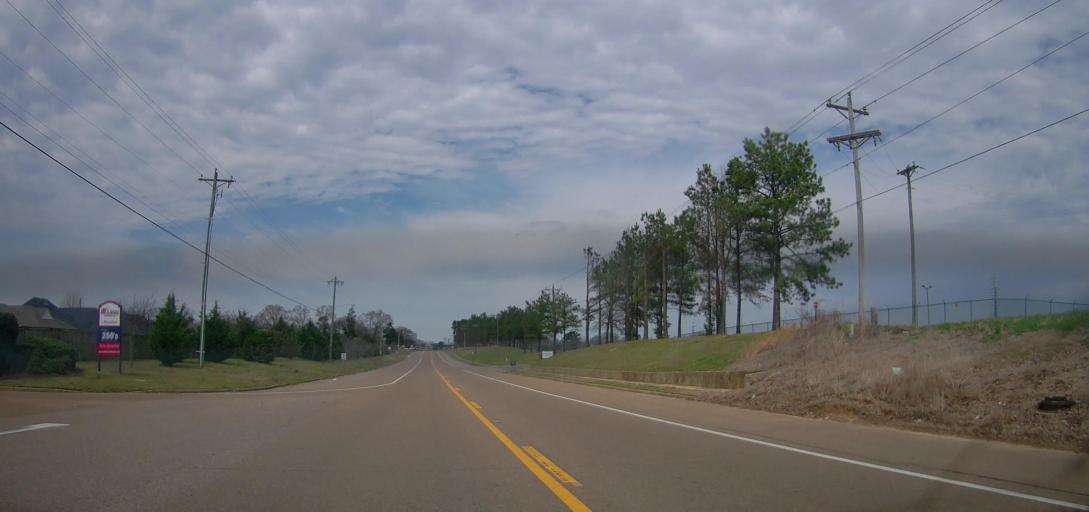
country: US
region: Mississippi
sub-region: De Soto County
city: Olive Branch
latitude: 34.9776
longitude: -89.8497
